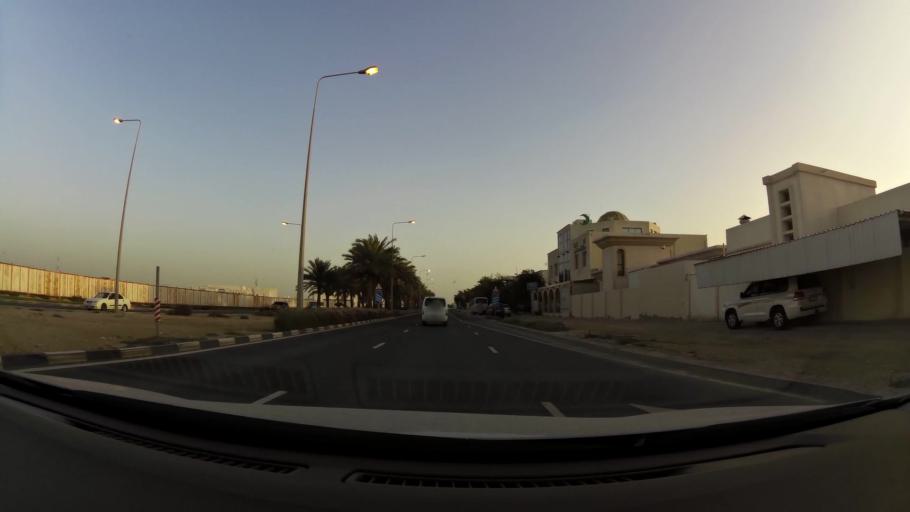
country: QA
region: Baladiyat ad Dawhah
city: Doha
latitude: 25.3179
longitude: 51.4866
